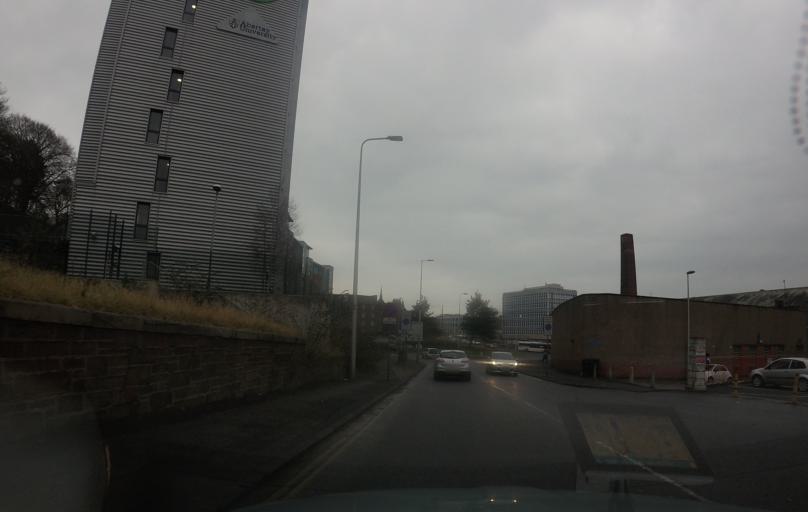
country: GB
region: Scotland
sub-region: Dundee City
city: Dundee
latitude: 56.4638
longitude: -2.9815
